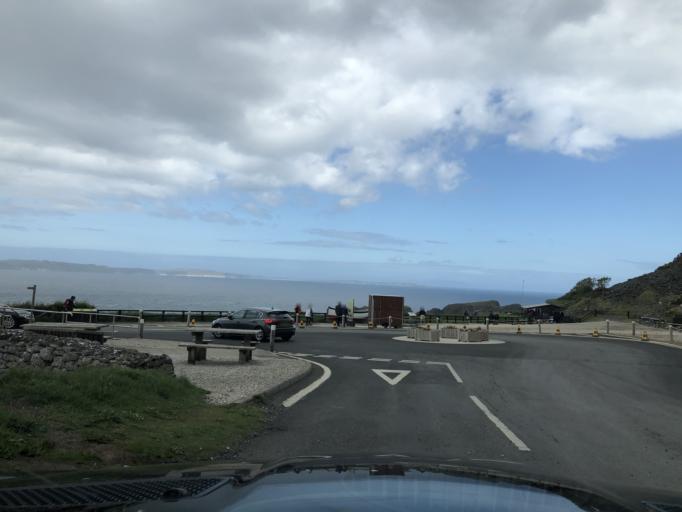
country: GB
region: Northern Ireland
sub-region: Moyle District
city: Ballycastle
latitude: 55.2389
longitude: -6.3477
